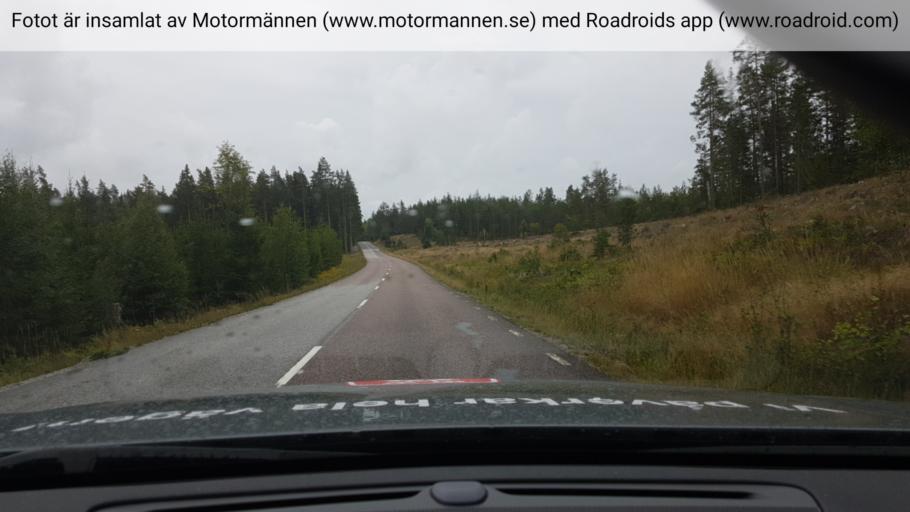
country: SE
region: Stockholm
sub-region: Botkyrka Kommun
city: Tullinge
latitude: 59.0926
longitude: 17.8901
